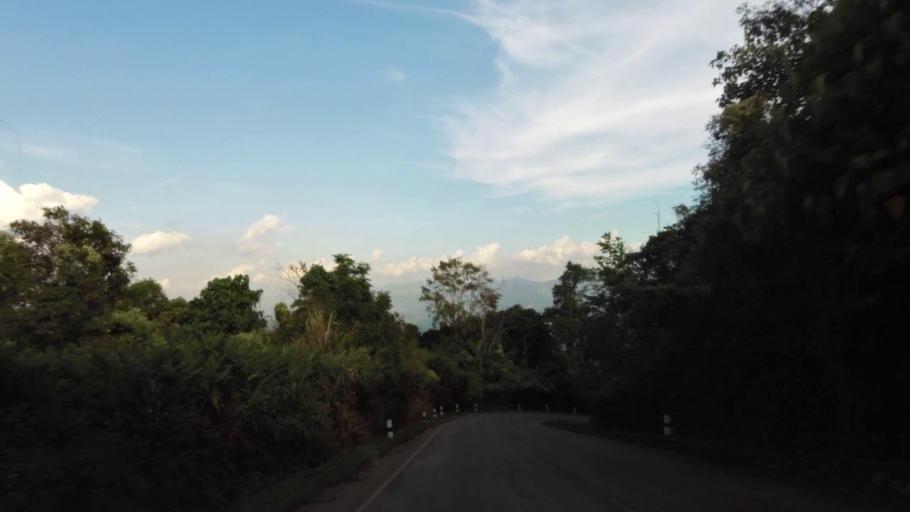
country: TH
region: Chiang Rai
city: Khun Tan
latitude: 19.8735
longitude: 100.3445
